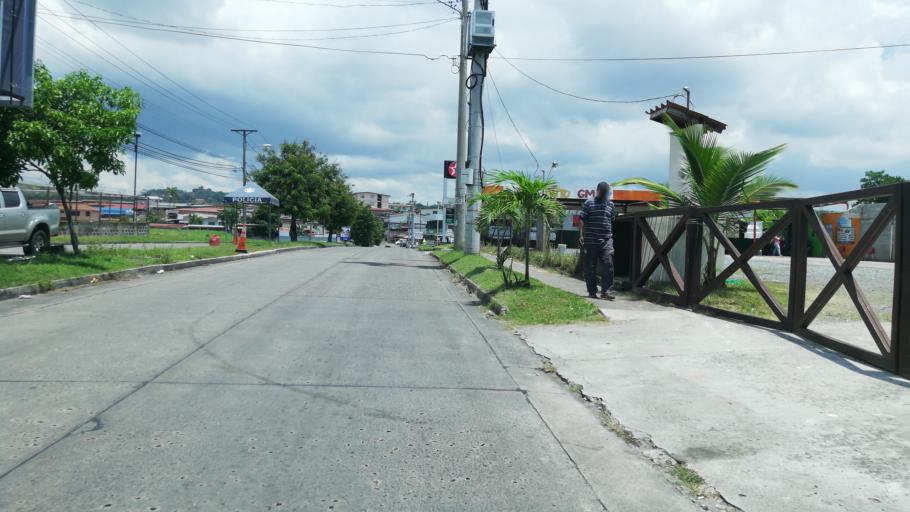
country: PA
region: Panama
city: San Miguelito
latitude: 9.0524
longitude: -79.4544
